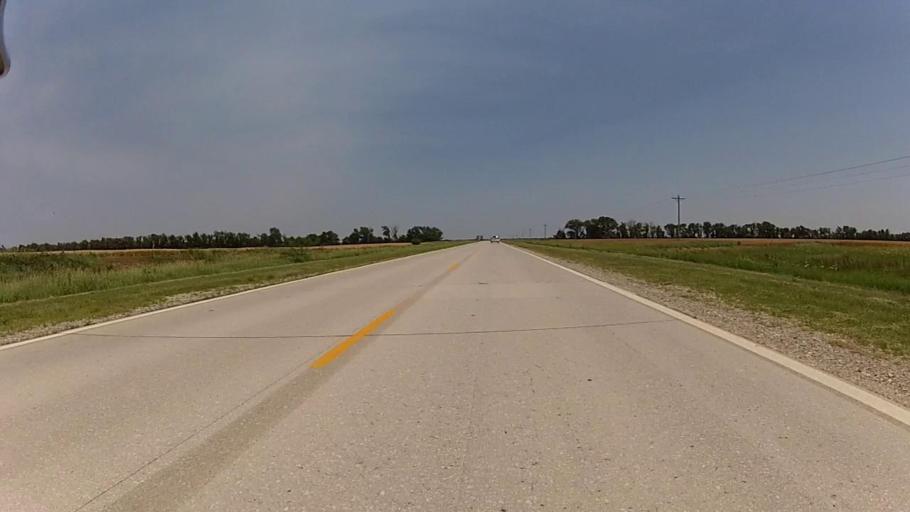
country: US
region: Kansas
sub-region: Cowley County
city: Arkansas City
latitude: 37.0575
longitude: -97.2677
